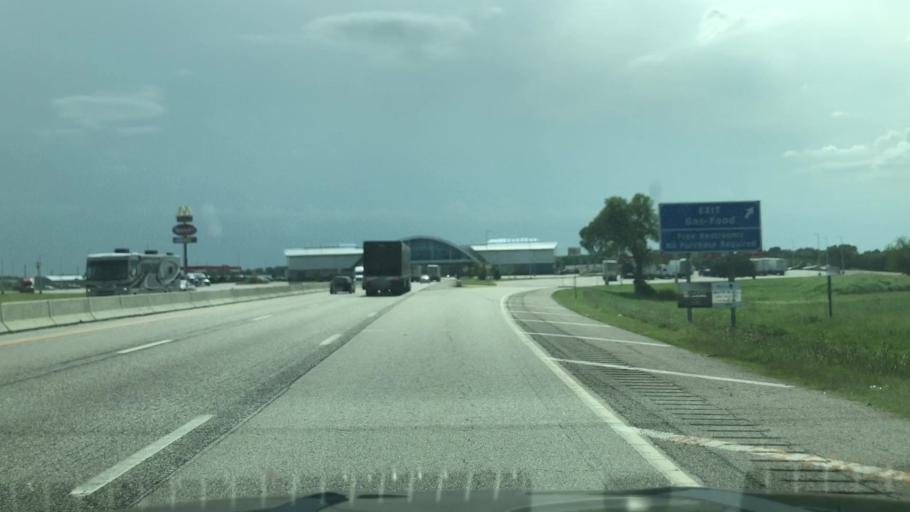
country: US
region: Oklahoma
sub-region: Craig County
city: Vinita
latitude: 36.6247
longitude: -95.1452
